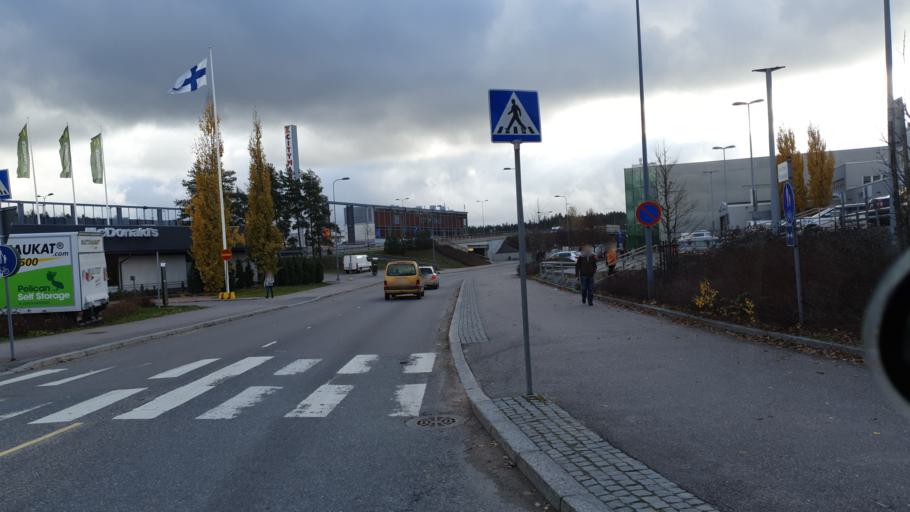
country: FI
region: Uusimaa
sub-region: Helsinki
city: Kirkkonummi
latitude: 60.1217
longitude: 24.4407
